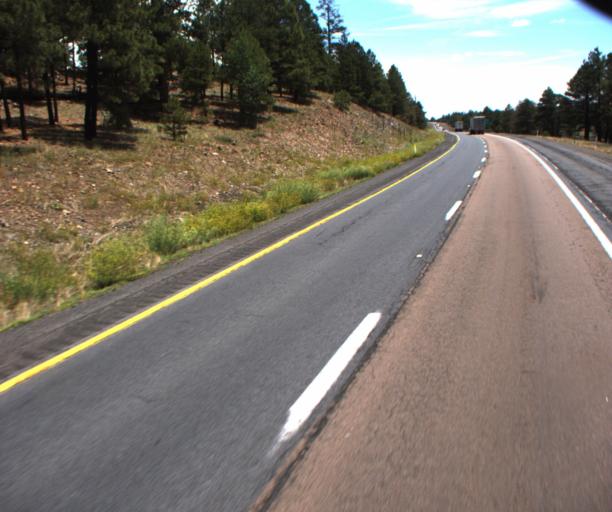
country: US
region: Arizona
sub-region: Coconino County
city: Flagstaff
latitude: 35.2034
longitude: -111.7666
